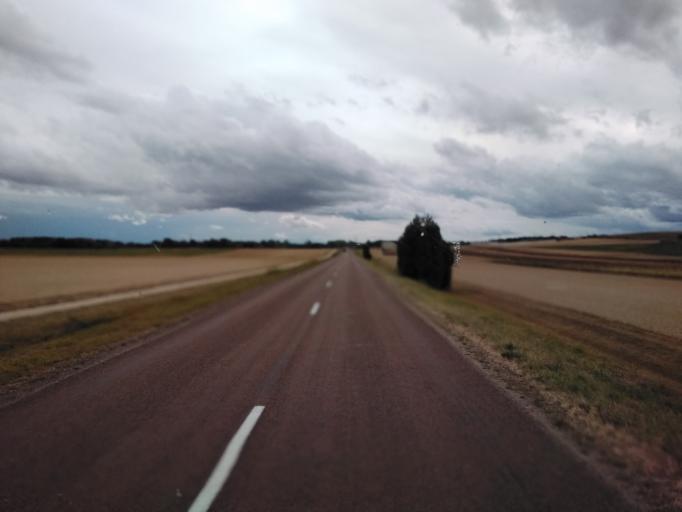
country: FR
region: Champagne-Ardenne
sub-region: Departement de l'Aube
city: Brienne-le-Chateau
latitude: 48.4761
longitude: 4.5052
